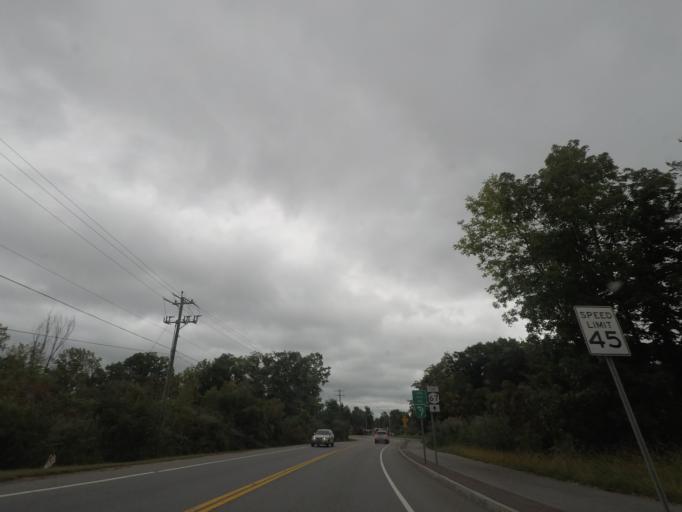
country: US
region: New York
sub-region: Saratoga County
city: Country Knolls
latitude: 42.9480
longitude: -73.7871
